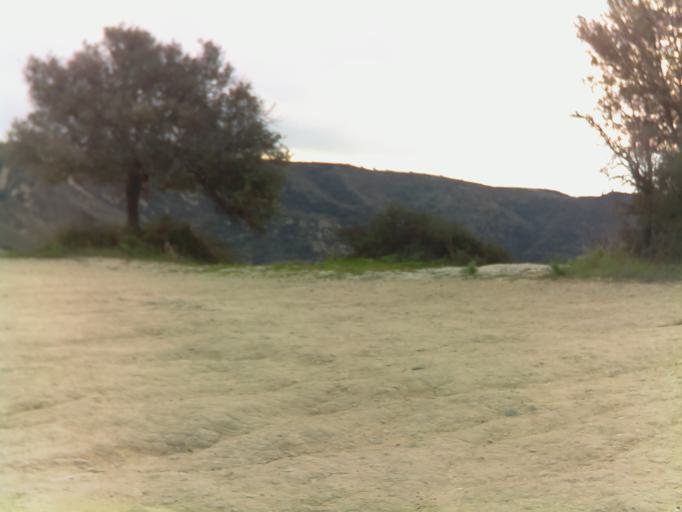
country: CY
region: Pafos
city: Pegeia
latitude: 34.9029
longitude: 32.4081
